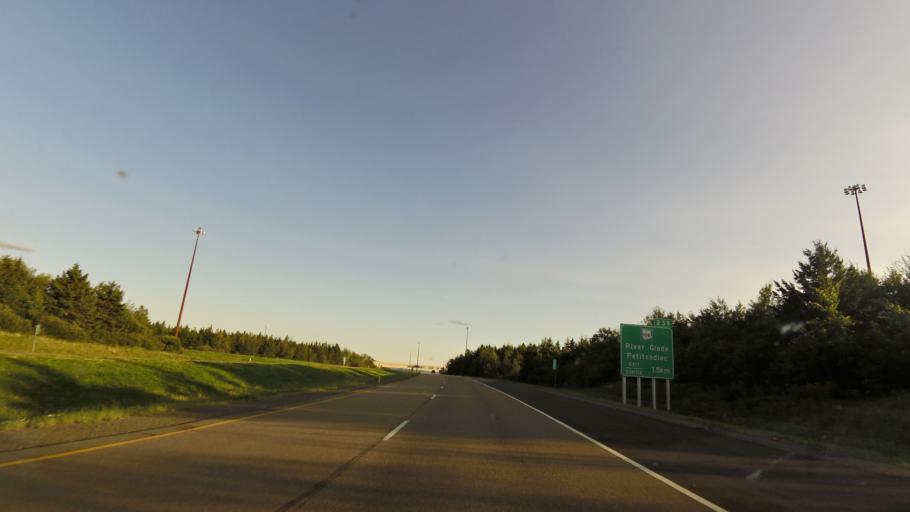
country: CA
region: New Brunswick
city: Salisbury
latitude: 45.9906
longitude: -65.1388
